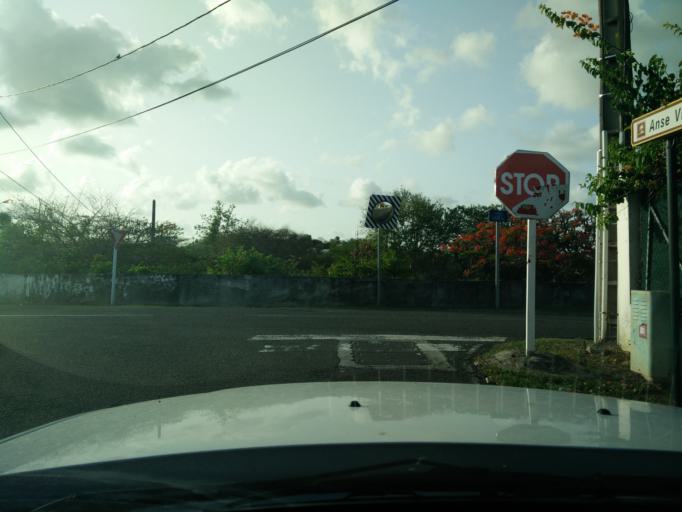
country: GP
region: Guadeloupe
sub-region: Guadeloupe
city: Le Gosier
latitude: 16.2022
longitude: -61.4717
